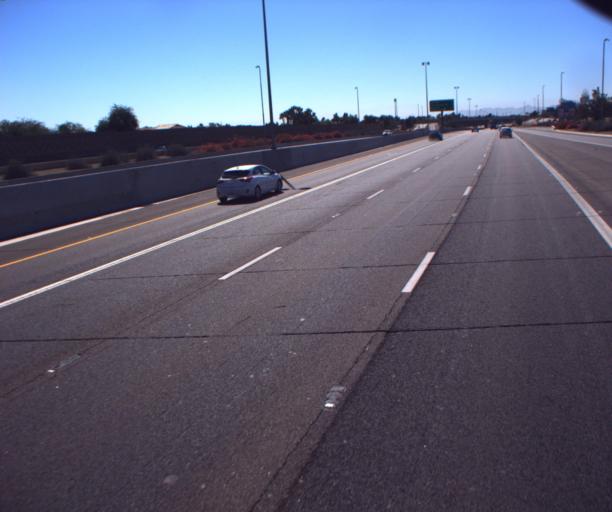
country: US
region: Arizona
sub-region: Maricopa County
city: Sun City
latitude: 33.6587
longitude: -112.2326
